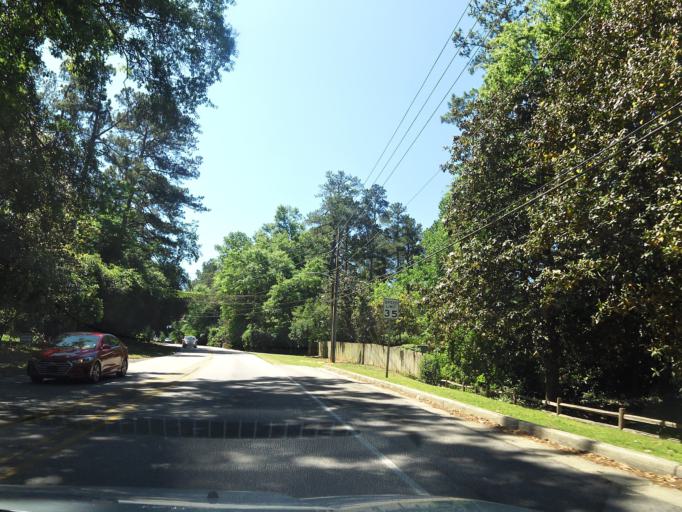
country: US
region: Georgia
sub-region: Columbia County
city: Martinez
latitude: 33.4929
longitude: -82.0304
